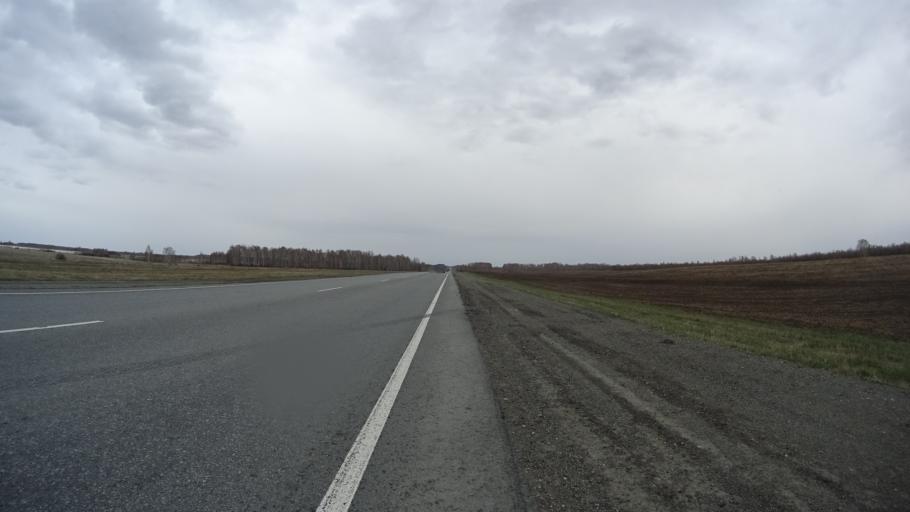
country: RU
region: Chelyabinsk
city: Krasnogorskiy
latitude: 54.6632
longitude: 61.2539
